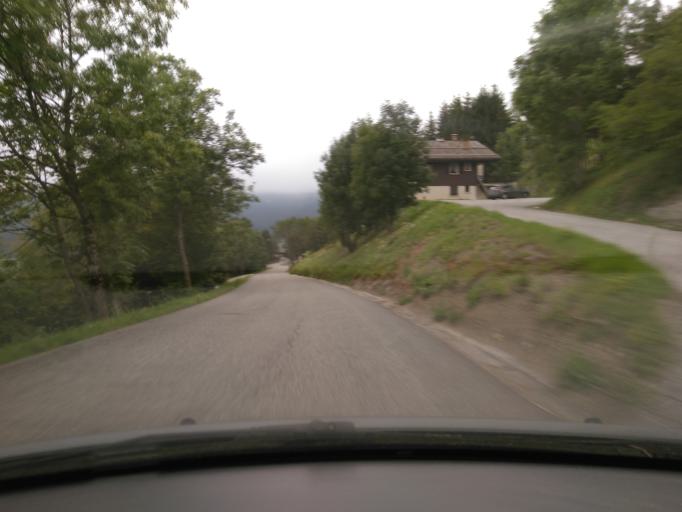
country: FR
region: Rhone-Alpes
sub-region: Departement de la Haute-Savoie
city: La Clusaz
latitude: 45.9107
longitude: 6.4403
